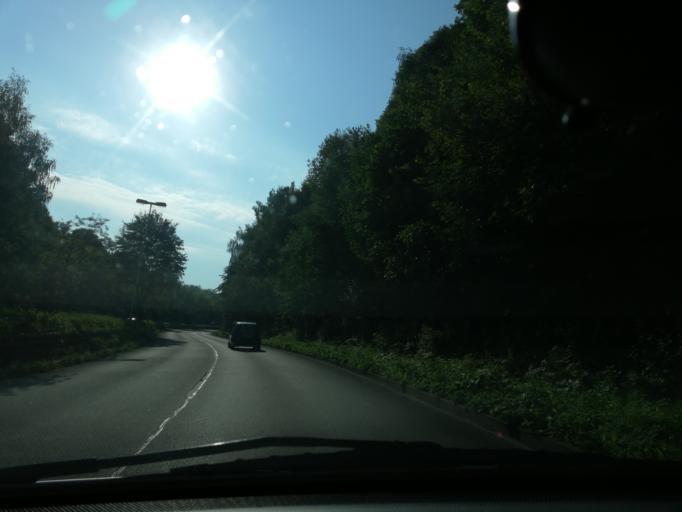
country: DE
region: North Rhine-Westphalia
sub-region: Regierungsbezirk Dusseldorf
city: Wuppertal
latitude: 51.2445
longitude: 7.1654
